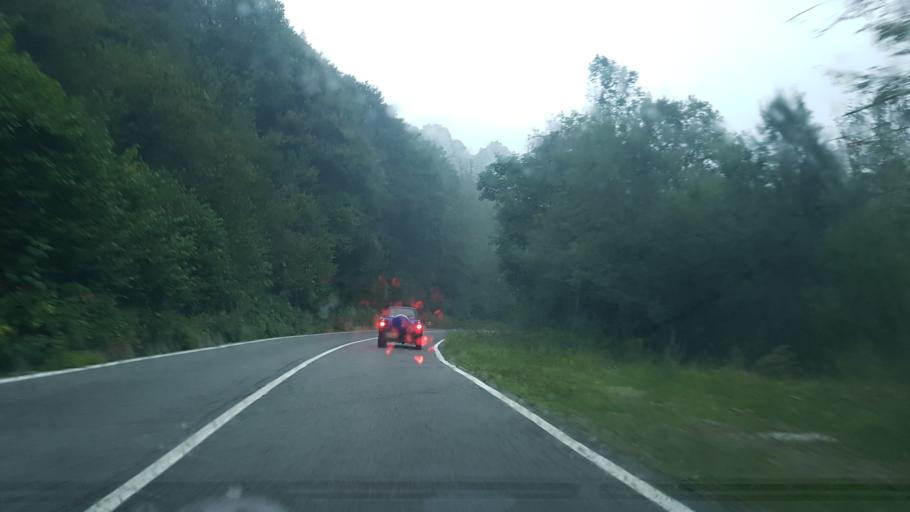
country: IT
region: Piedmont
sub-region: Provincia di Cuneo
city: Frabosa Soprana
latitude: 44.2644
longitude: 7.7660
